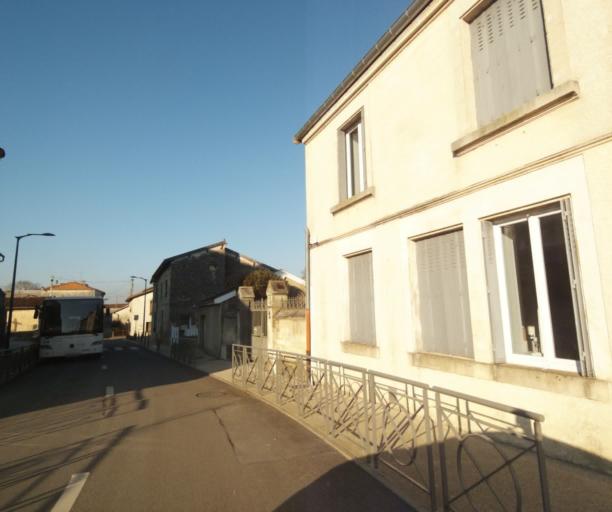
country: FR
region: Champagne-Ardenne
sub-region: Departement de la Haute-Marne
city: Bienville
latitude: 48.5721
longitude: 5.0459
